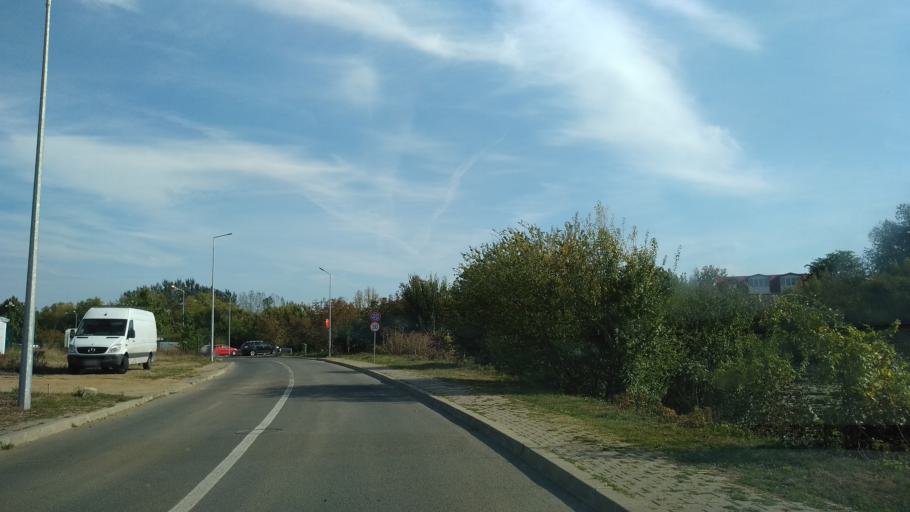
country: RO
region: Ilfov
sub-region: Comuna Chitila
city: Chitila
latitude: 44.5122
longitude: 25.9854
